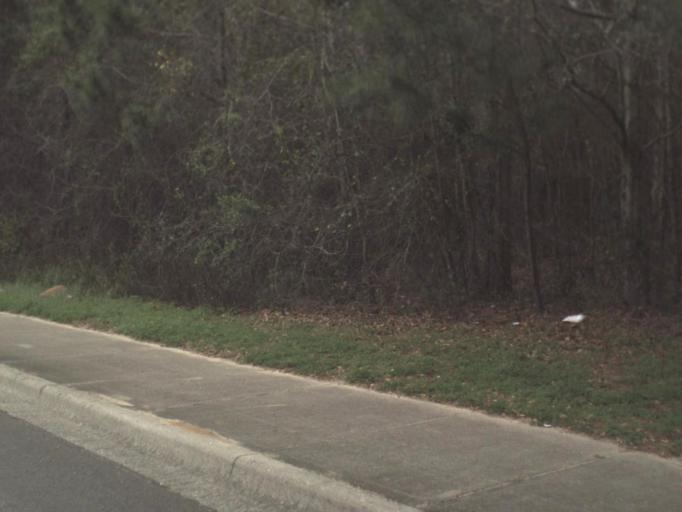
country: US
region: Florida
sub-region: Leon County
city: Tallahassee
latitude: 30.5287
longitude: -84.2352
